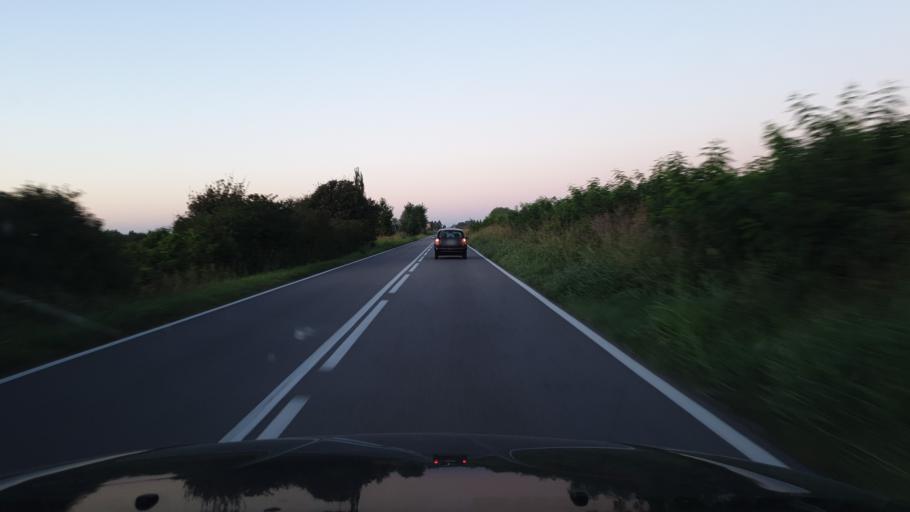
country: IT
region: Emilia-Romagna
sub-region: Provincia di Bologna
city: Minerbio
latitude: 44.6343
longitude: 11.4676
